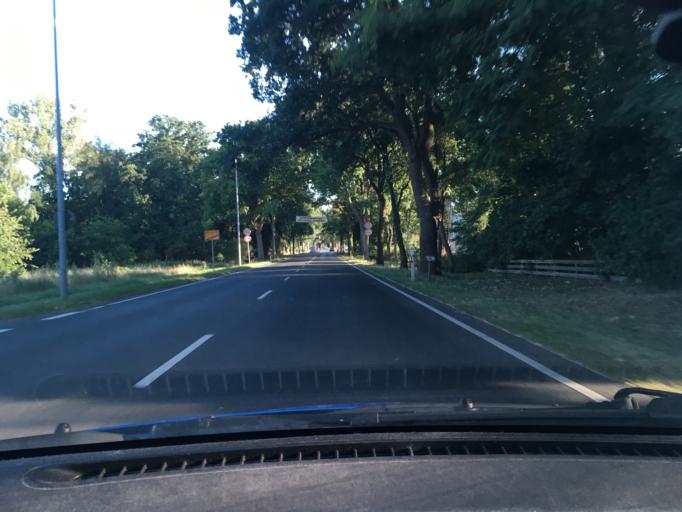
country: DE
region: Lower Saxony
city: Celle
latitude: 52.5951
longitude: 10.0691
